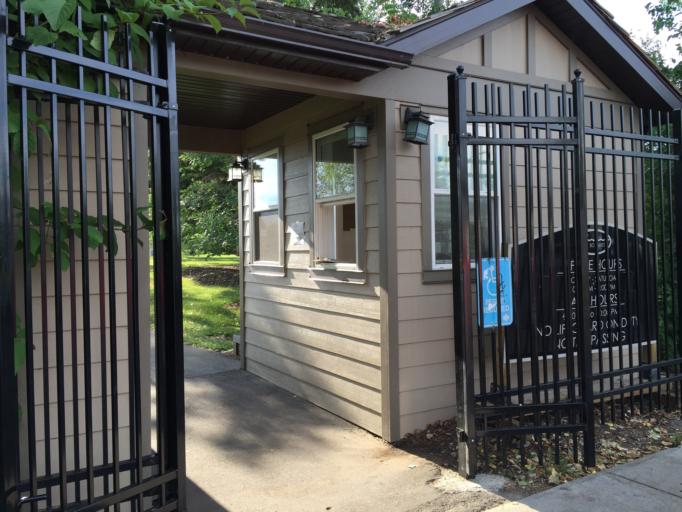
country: CA
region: Alberta
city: Calgary
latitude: 50.9387
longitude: -114.0482
